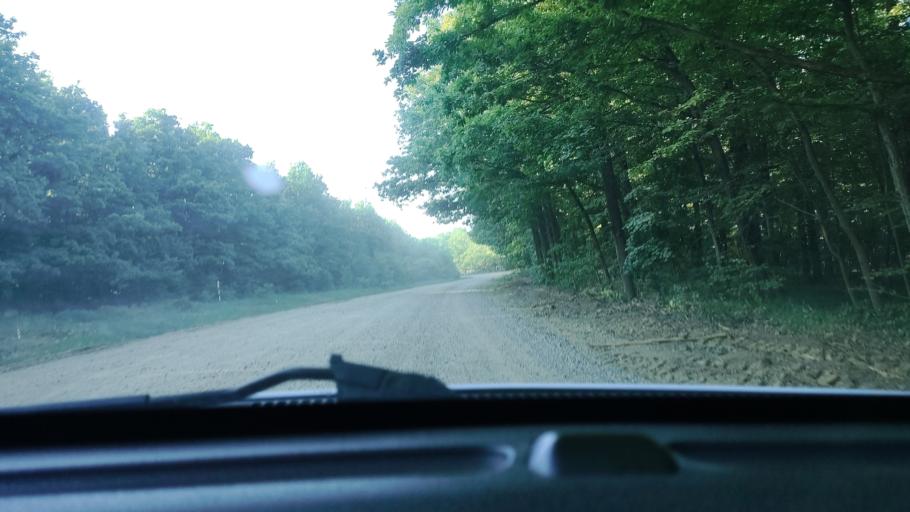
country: RU
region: Krasnodarskiy
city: Novodmitriyevskaya
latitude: 44.7161
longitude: 38.9914
